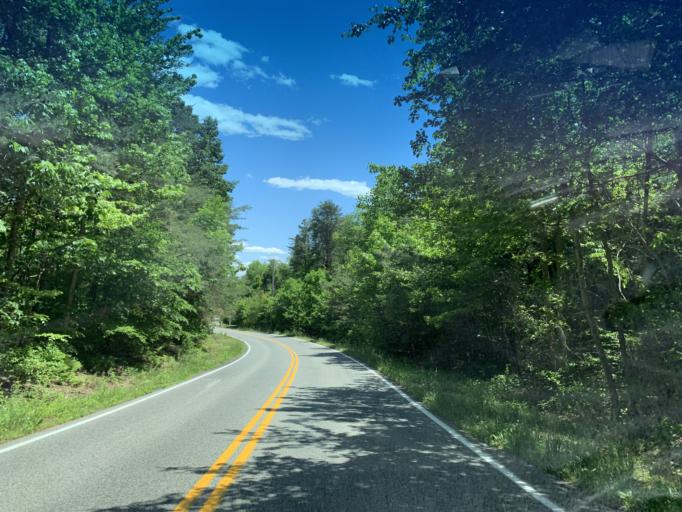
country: US
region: Maryland
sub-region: Cecil County
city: Charlestown
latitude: 39.6171
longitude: -75.9879
